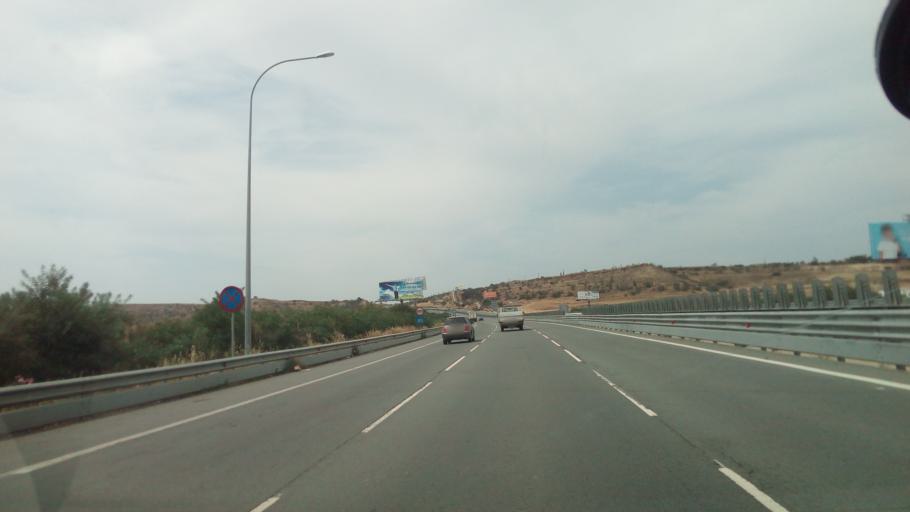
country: CY
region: Lefkosia
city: Dali
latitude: 35.0550
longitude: 33.3851
